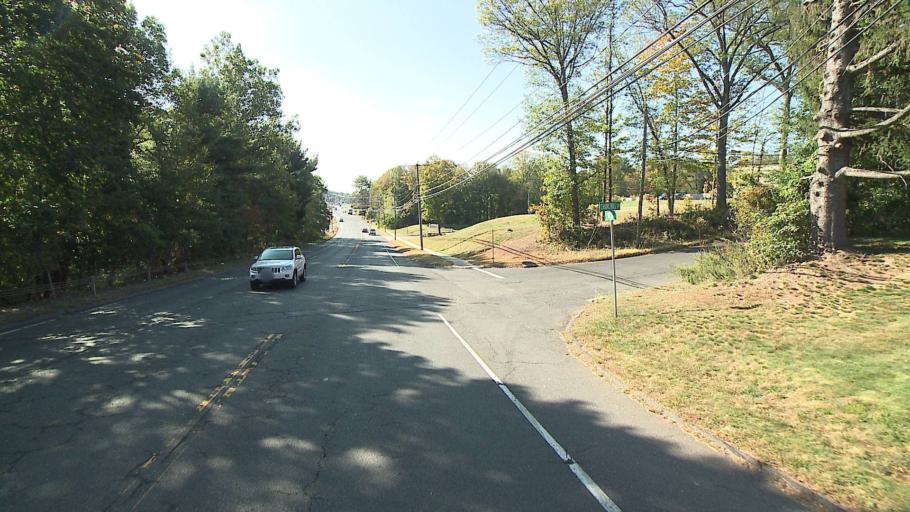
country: US
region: Connecticut
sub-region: Hartford County
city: Plainville
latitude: 41.6217
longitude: -72.8997
